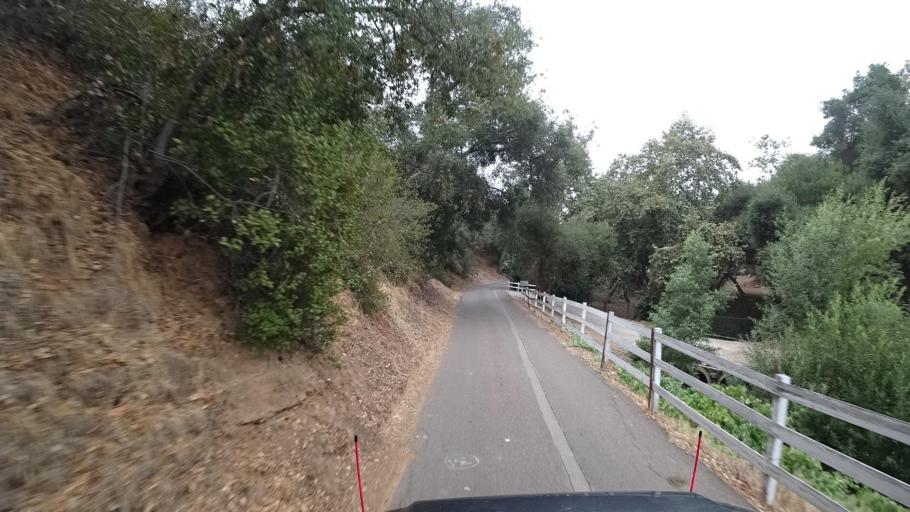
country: US
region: California
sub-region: San Diego County
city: Rainbow
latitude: 33.3829
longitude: -117.1636
